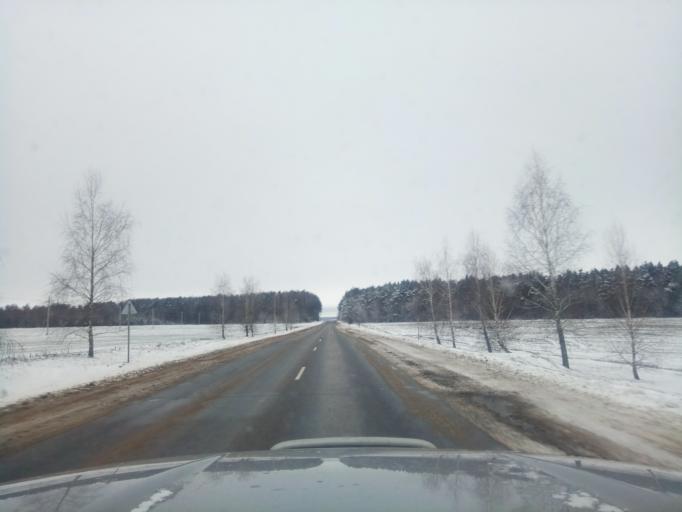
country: BY
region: Minsk
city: Kapyl'
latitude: 53.1555
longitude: 27.1139
